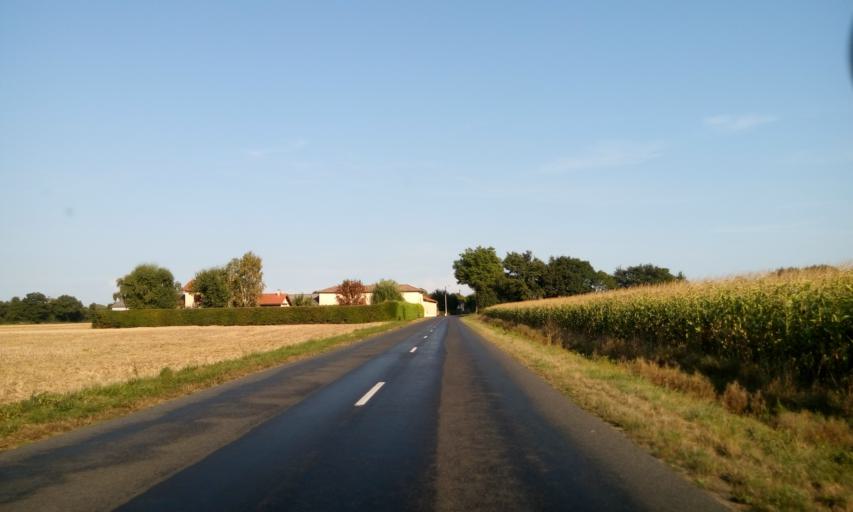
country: FR
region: Rhone-Alpes
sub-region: Departement de l'Ain
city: Amberieux-en-Dombes
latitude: 45.9999
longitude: 4.8901
